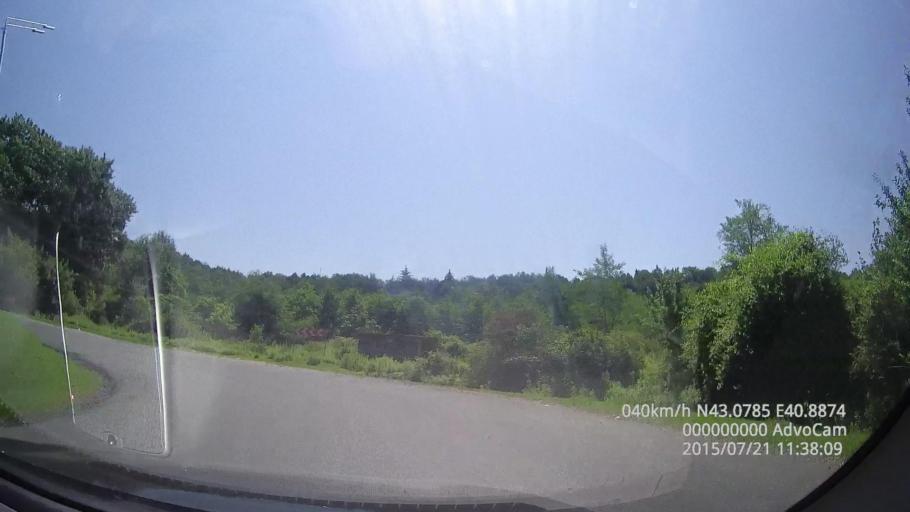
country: GE
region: Abkhazia
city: Stantsiya Novyy Afon
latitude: 43.0785
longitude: 40.8876
